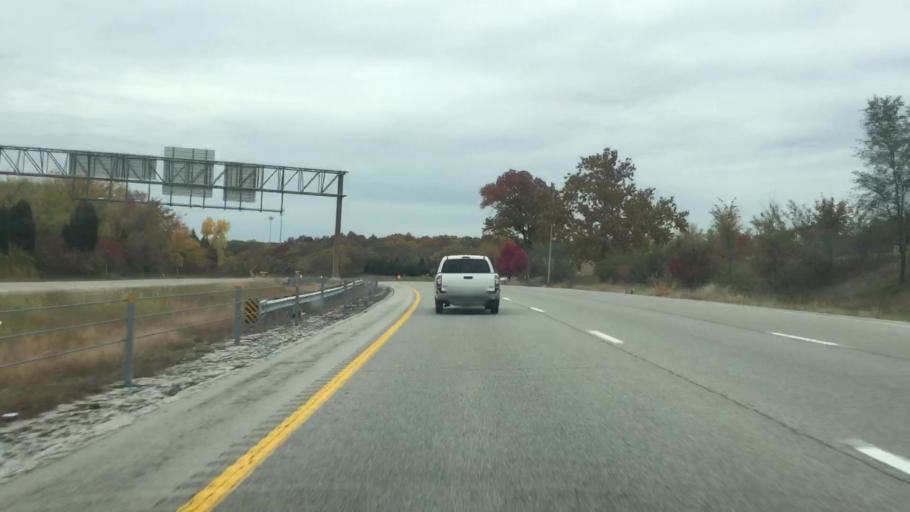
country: US
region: Missouri
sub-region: Jackson County
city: Lees Summit
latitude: 38.9474
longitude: -94.4099
